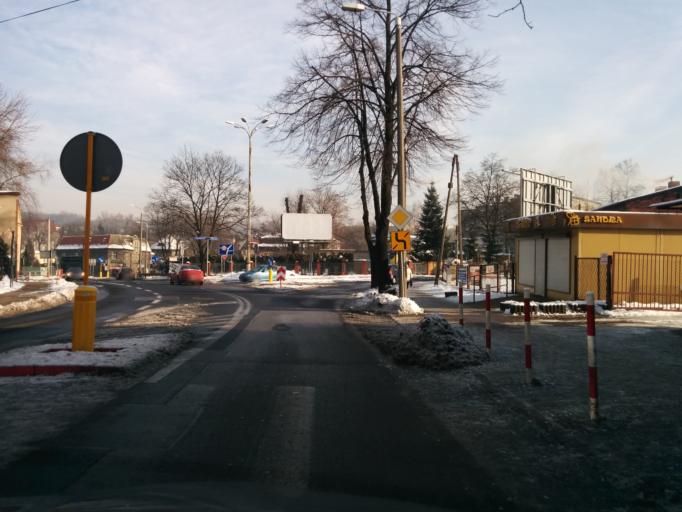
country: PL
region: Silesian Voivodeship
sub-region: Ruda Slaska
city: Ruda Slaska
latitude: 50.2683
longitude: 18.8375
